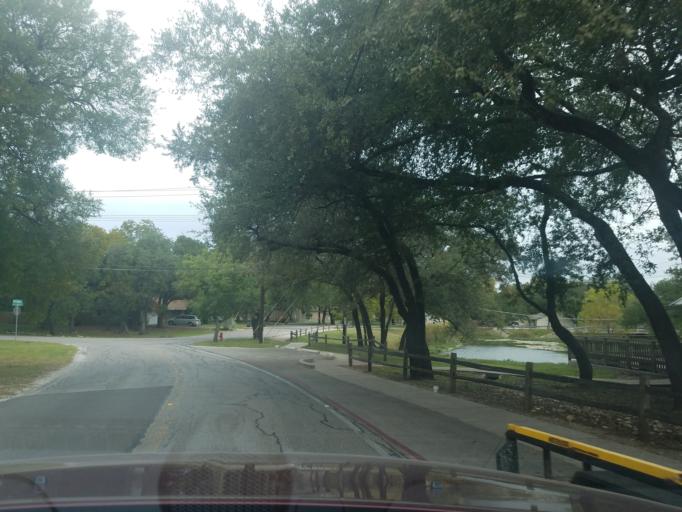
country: US
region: Texas
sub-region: Williamson County
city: Anderson Mill
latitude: 30.4791
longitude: -97.8131
